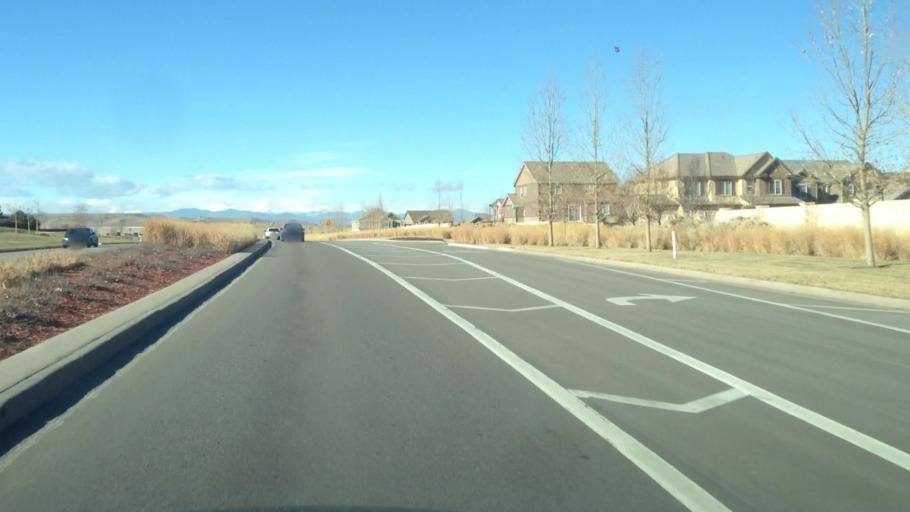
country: US
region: Colorado
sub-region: Douglas County
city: Stonegate
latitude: 39.5198
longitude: -104.8264
